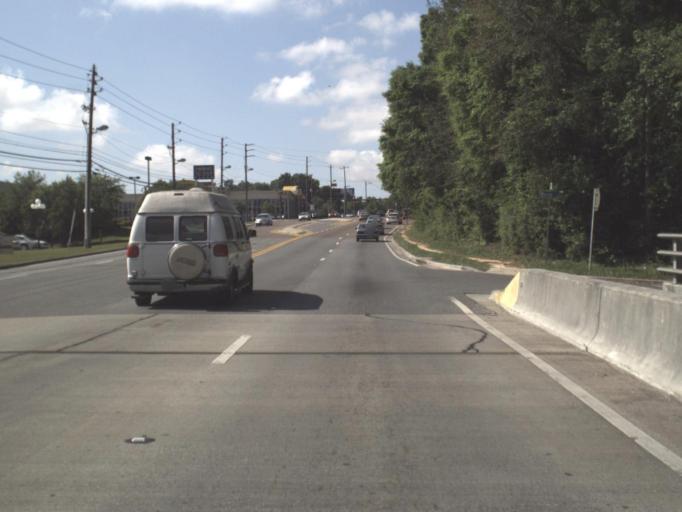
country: US
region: Florida
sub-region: Escambia County
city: Brent
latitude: 30.4842
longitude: -87.2228
